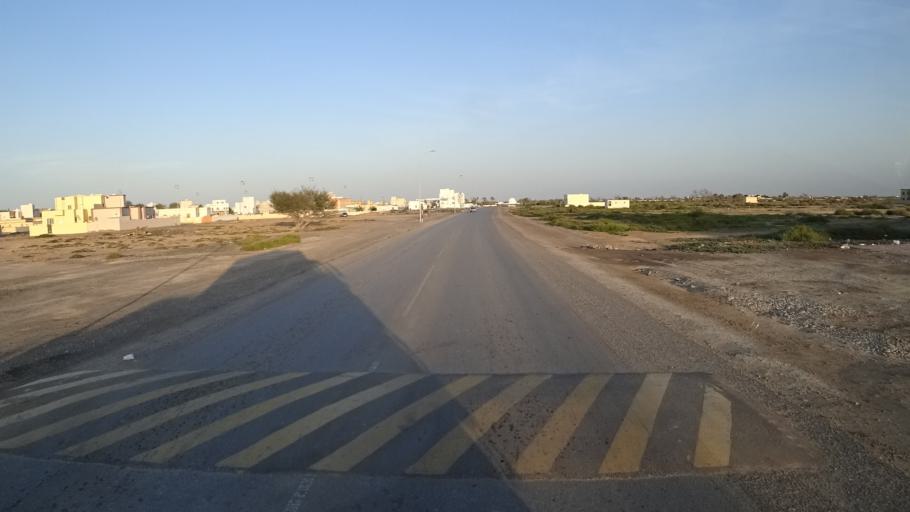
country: OM
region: Al Batinah
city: Barka'
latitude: 23.7022
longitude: 57.9333
